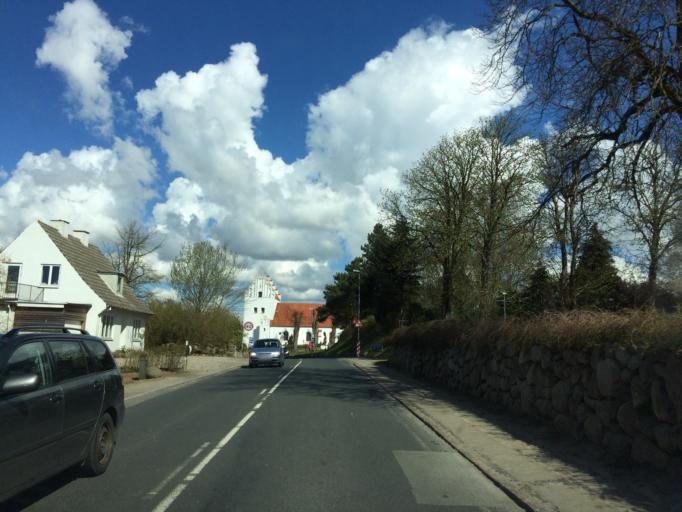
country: DK
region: South Denmark
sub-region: Assens Kommune
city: Harby
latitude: 55.1987
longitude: 10.1568
